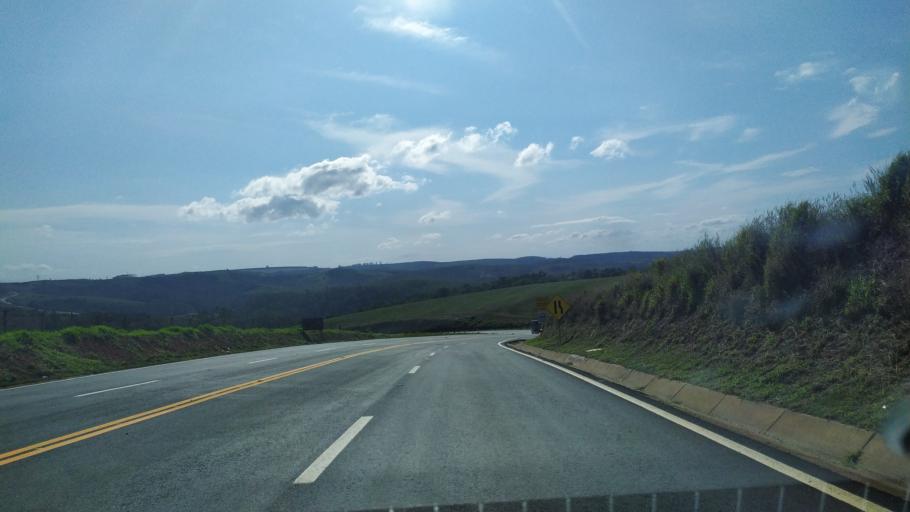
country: BR
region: Parana
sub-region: Telemaco Borba
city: Telemaco Borba
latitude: -24.2800
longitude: -50.7139
